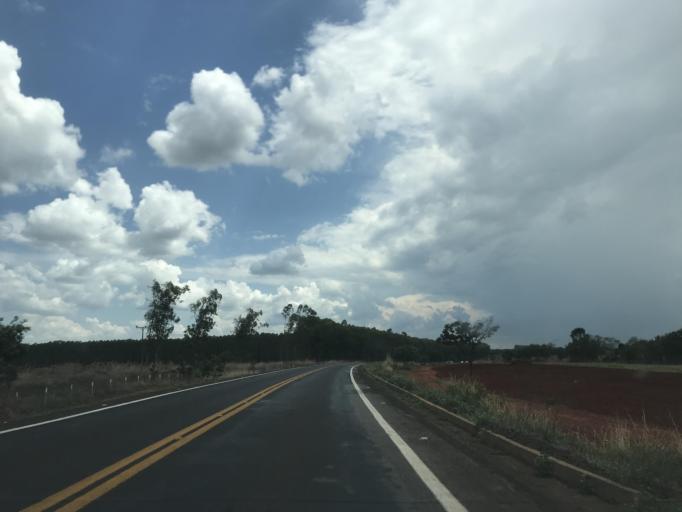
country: BR
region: Goias
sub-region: Caldas Novas
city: Caldas Novas
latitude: -17.6403
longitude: -48.7035
